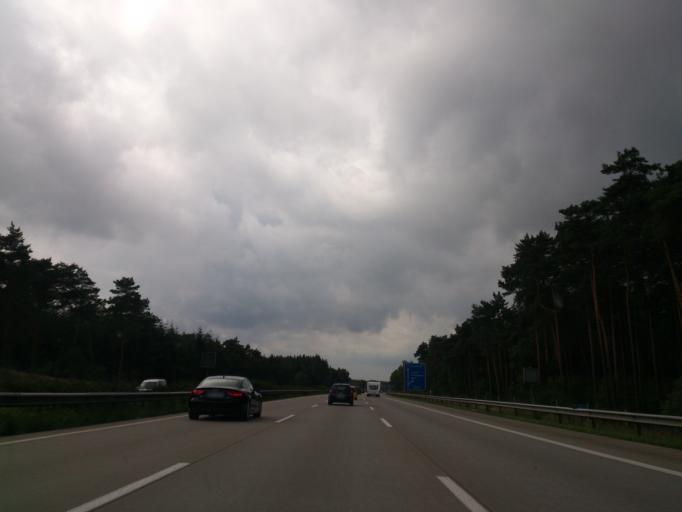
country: DE
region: Lower Saxony
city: Egestorf
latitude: 53.1702
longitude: 10.0741
